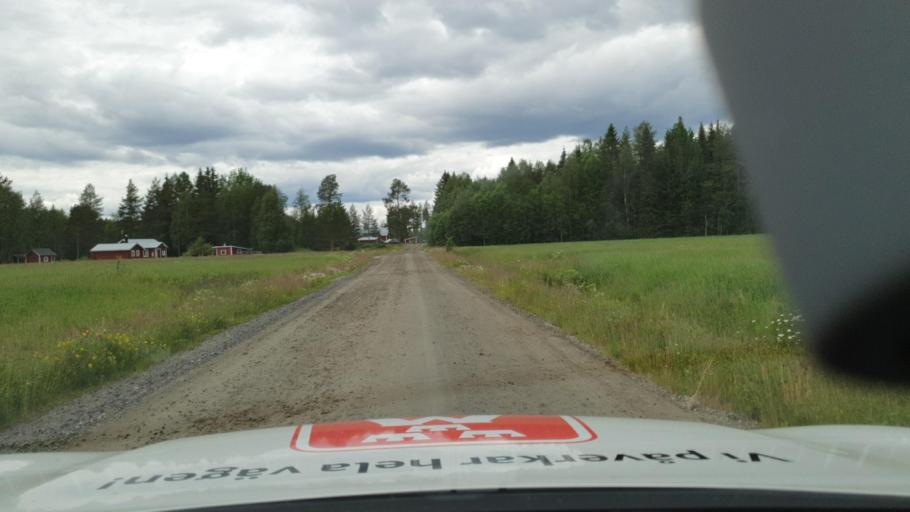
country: SE
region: Vaesterbotten
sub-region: Bjurholms Kommun
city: Bjurholm
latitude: 63.7946
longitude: 19.0926
